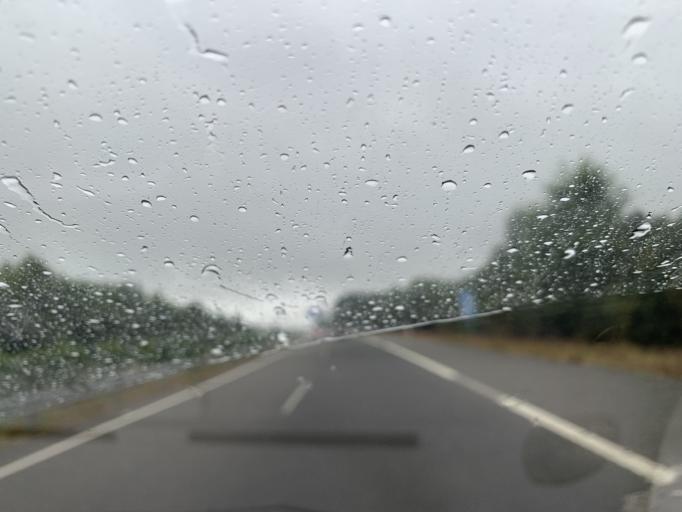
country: ES
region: Galicia
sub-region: Provincia de Lugo
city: Vilalba
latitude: 43.3273
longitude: -7.6142
